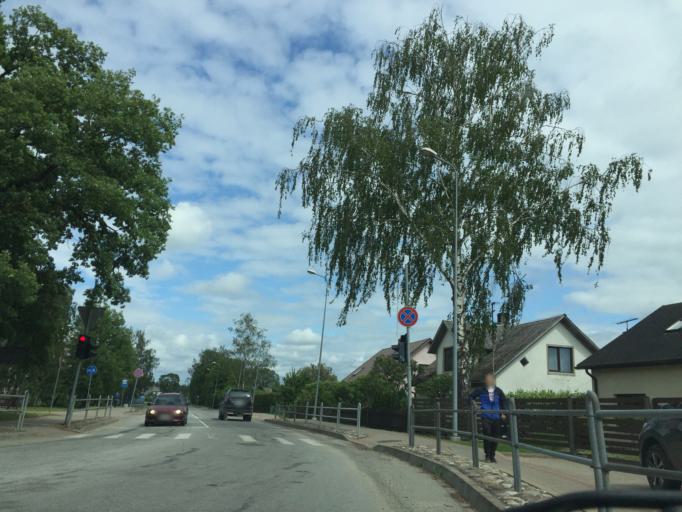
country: LV
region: Valmieras Rajons
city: Valmiera
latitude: 57.5485
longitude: 25.4343
